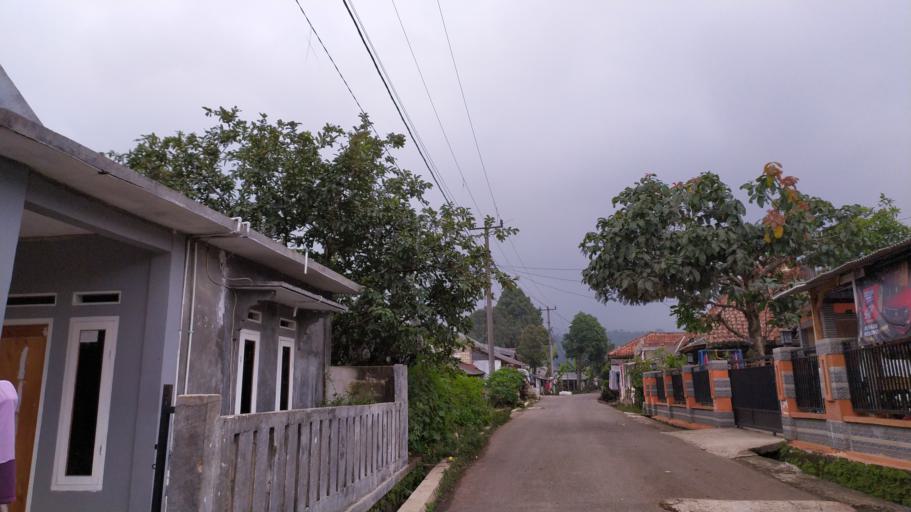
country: ID
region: West Java
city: Ciampea
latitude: -6.6383
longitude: 106.7071
